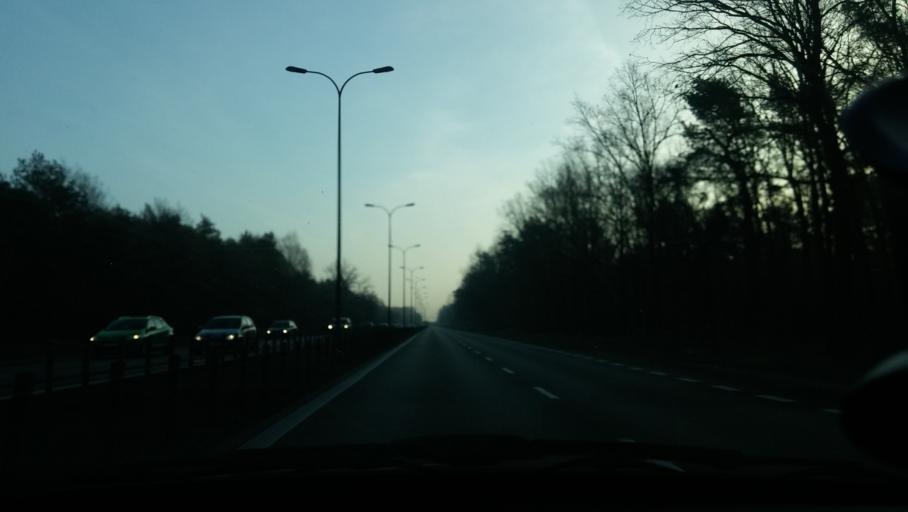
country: PL
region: Masovian Voivodeship
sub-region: Warszawa
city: Wawer
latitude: 52.2245
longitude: 21.1998
